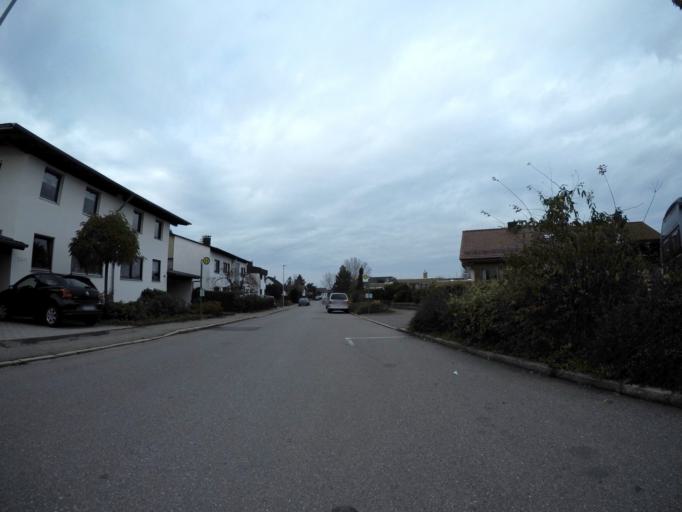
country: DE
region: Baden-Wuerttemberg
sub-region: Tuebingen Region
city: Reutlingen
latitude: 48.5018
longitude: 9.2305
